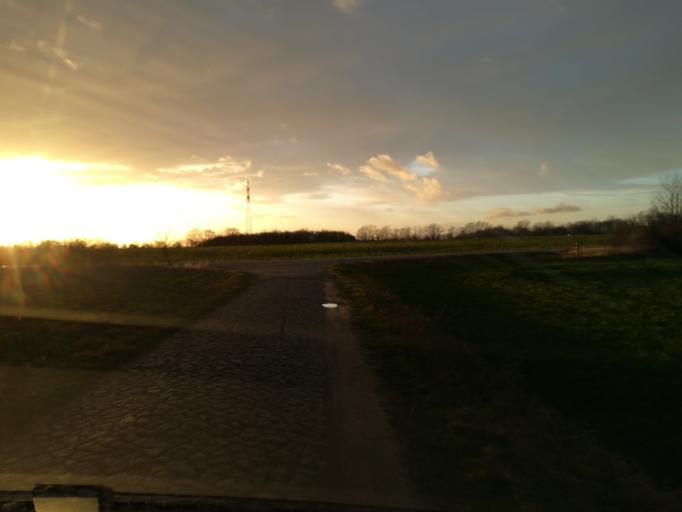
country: DE
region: Saxony-Anhalt
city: Brehna
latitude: 51.5174
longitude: 12.2031
